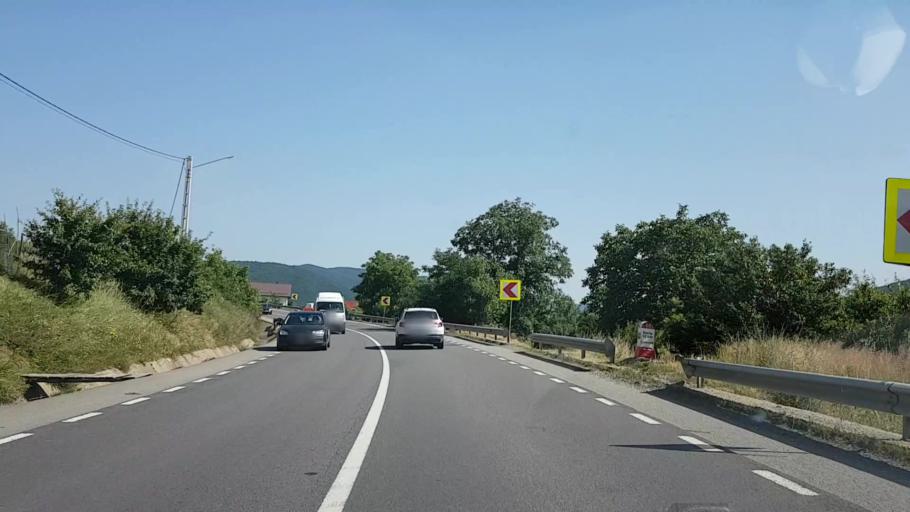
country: RO
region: Bistrita-Nasaud
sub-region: Comuna Sieu-Magherus
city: Sieu-Magherus
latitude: 47.0741
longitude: 24.3994
